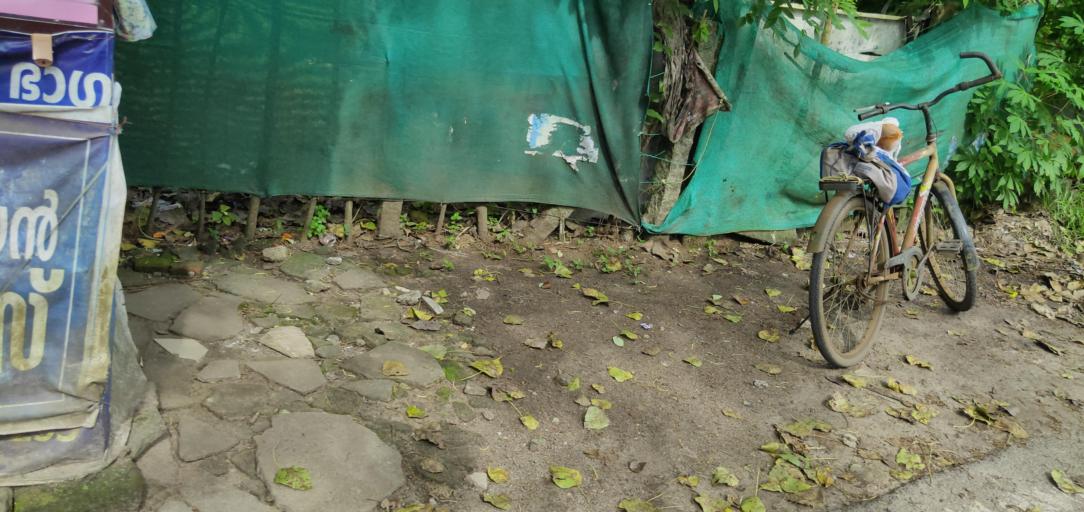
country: IN
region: Kerala
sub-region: Alappuzha
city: Kayankulam
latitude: 9.2335
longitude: 76.4564
